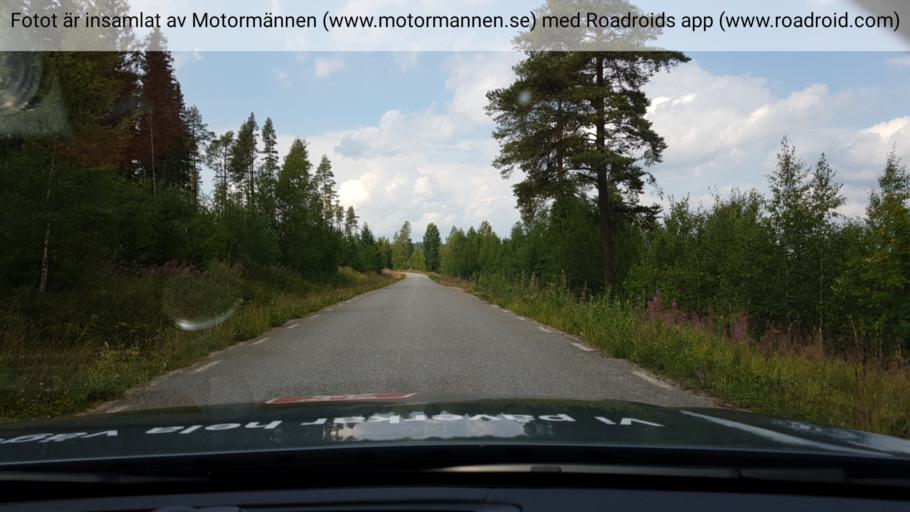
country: SE
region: Jaemtland
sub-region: OEstersunds Kommun
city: Brunflo
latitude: 62.9935
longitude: 15.1154
